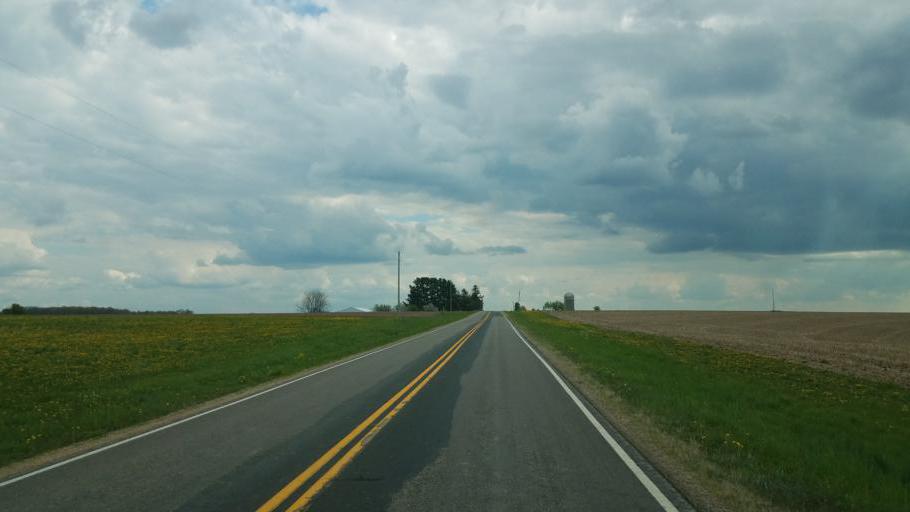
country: US
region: Wisconsin
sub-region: Vernon County
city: Hillsboro
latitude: 43.5677
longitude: -90.3312
